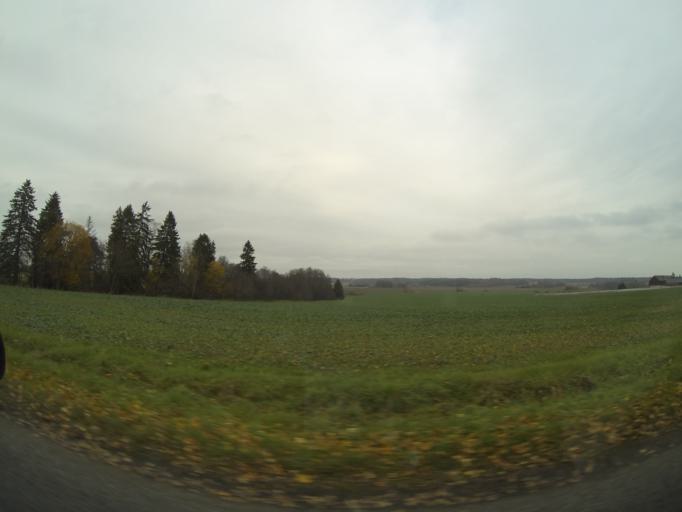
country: SE
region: Vaestmanland
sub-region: Vasteras
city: Skultuna
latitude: 59.6847
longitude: 16.4340
